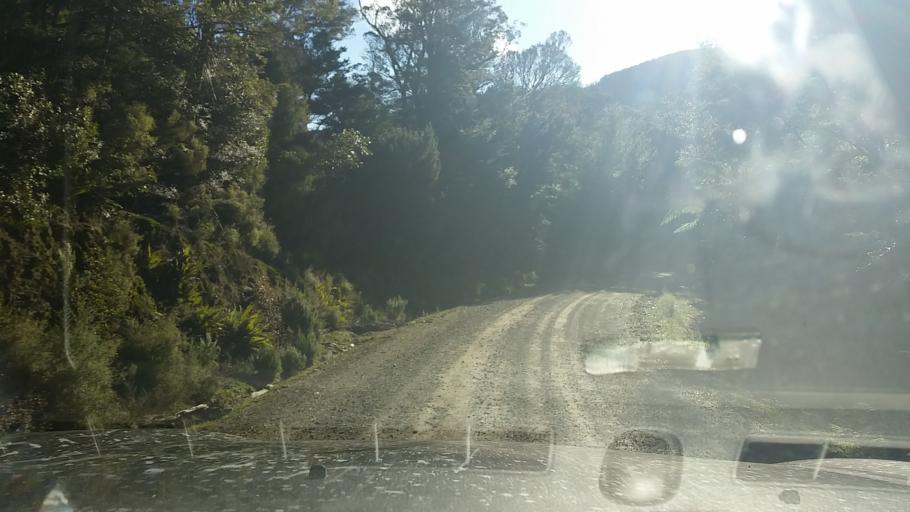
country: NZ
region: Marlborough
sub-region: Marlborough District
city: Picton
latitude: -41.0536
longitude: 174.1550
